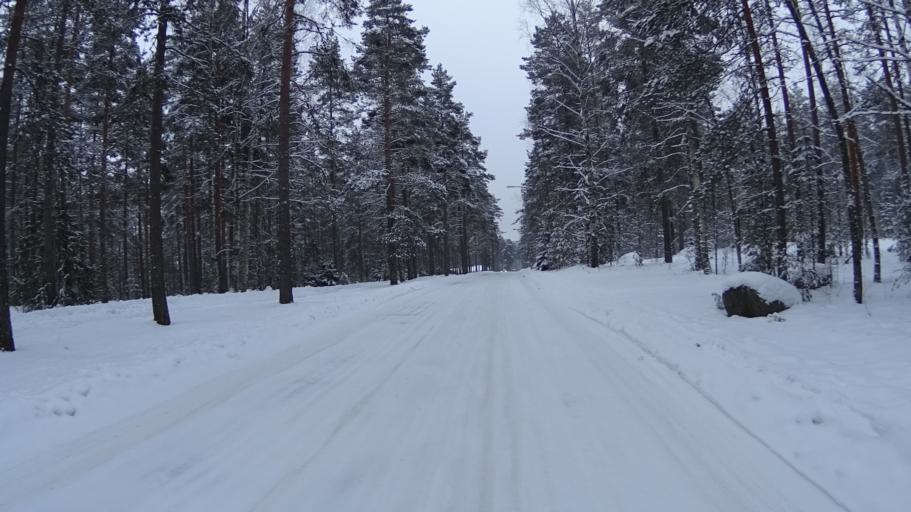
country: FI
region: Uusimaa
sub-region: Helsinki
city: Vihti
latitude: 60.3342
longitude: 24.2990
